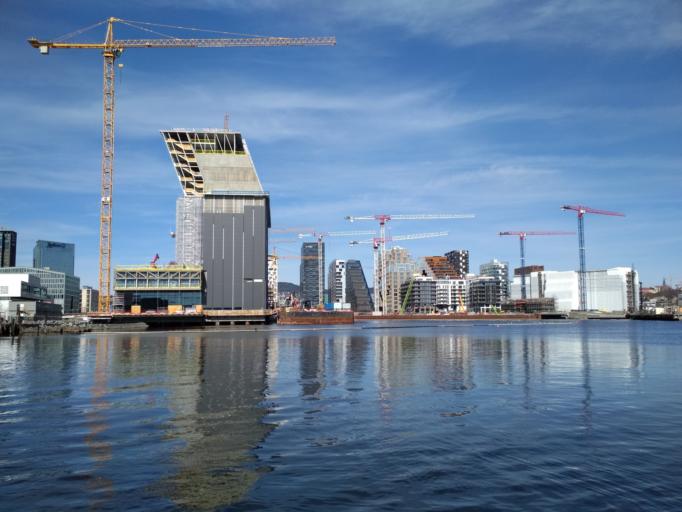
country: NO
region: Oslo
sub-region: Oslo
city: Oslo
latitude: 59.9037
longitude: 10.7540
